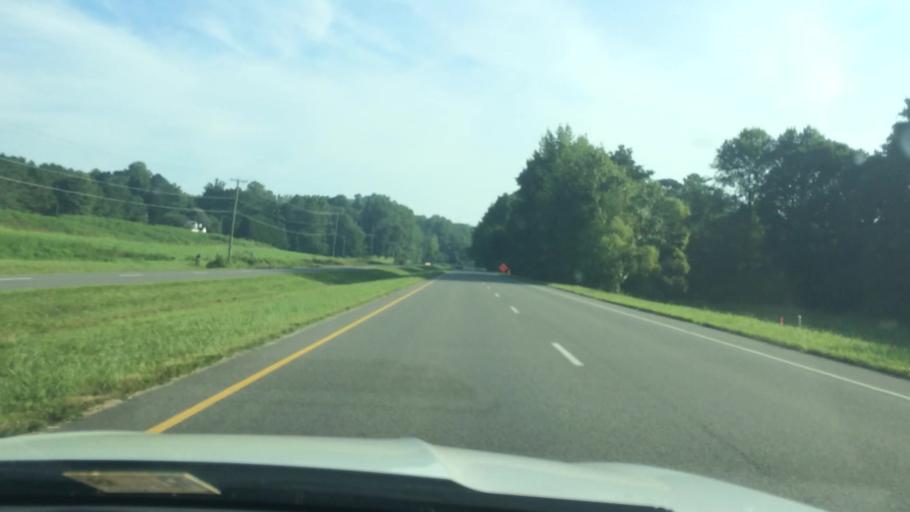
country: US
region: Virginia
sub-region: Gloucester County
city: Gloucester Courthouse
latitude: 37.4457
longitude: -76.4736
